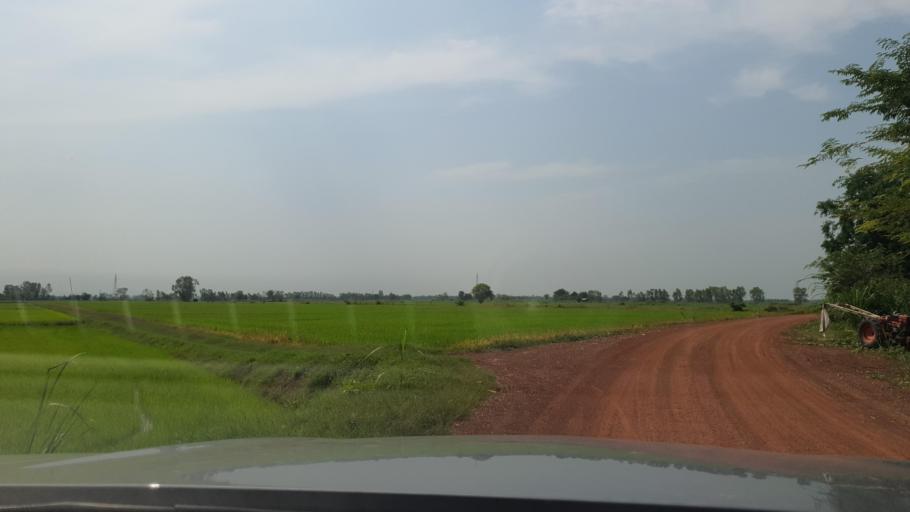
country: TH
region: Phitsanulok
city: Bang Rakam
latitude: 16.7925
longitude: 100.1090
